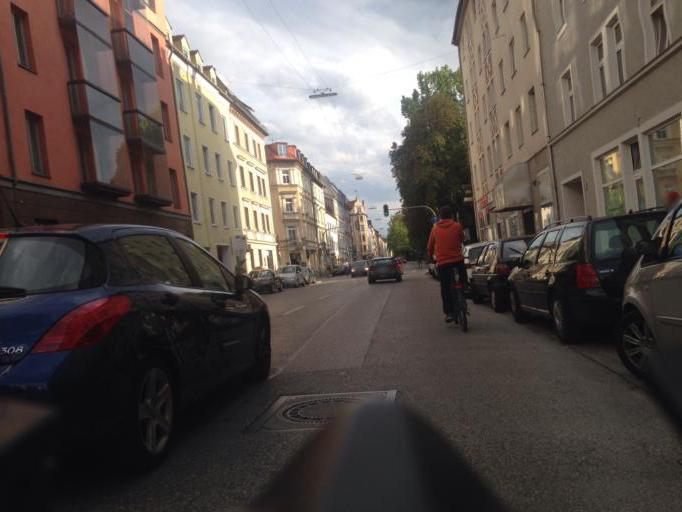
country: DE
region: Bavaria
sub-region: Upper Bavaria
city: Munich
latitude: 48.1540
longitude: 11.5610
